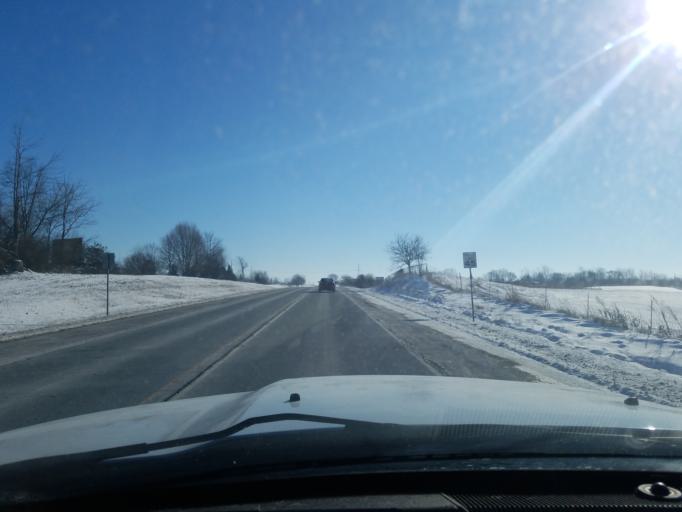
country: US
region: Indiana
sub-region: Noble County
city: Kendallville
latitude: 41.4499
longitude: -85.2421
